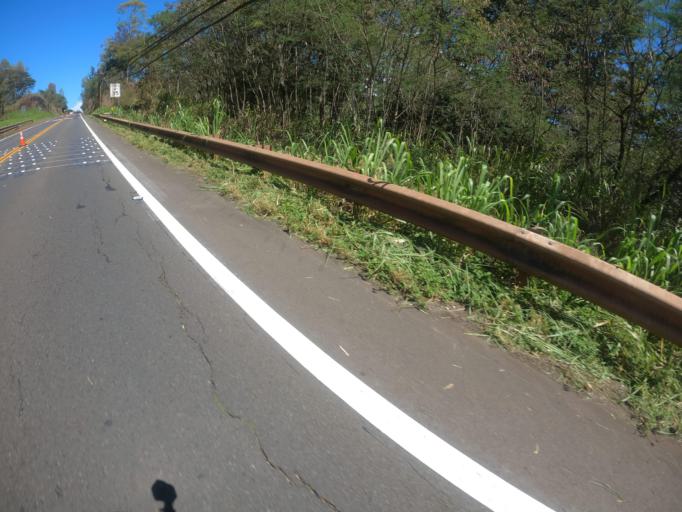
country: US
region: Hawaii
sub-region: Honolulu County
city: Schofield Barracks
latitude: 21.4770
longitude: -158.0504
